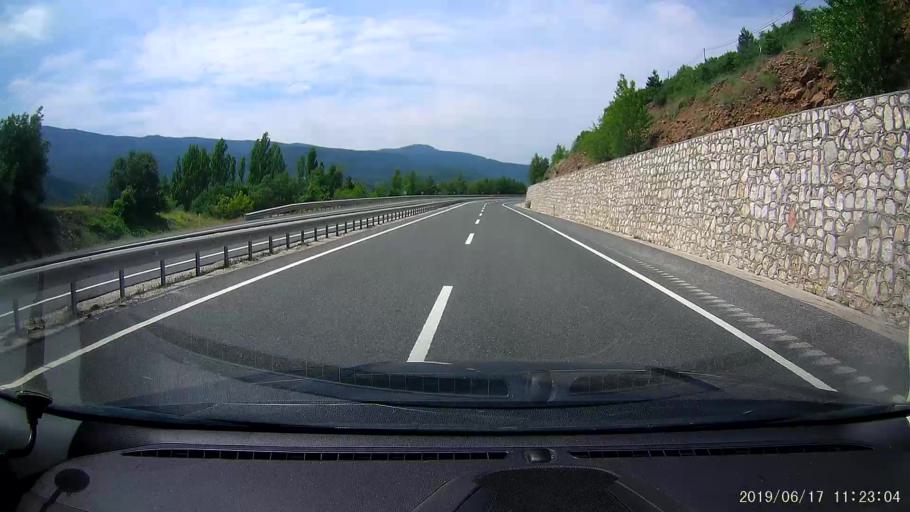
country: TR
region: Cankiri
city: Ilgaz
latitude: 40.8928
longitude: 33.7393
